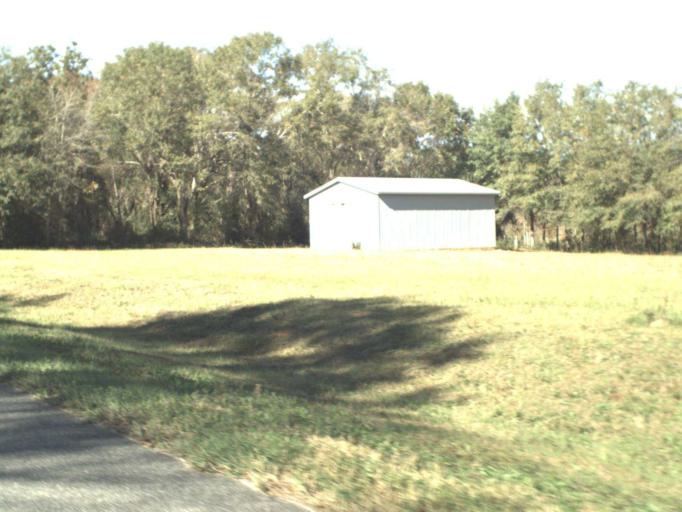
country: US
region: Florida
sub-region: Okaloosa County
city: Crestview
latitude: 30.8464
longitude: -86.7448
